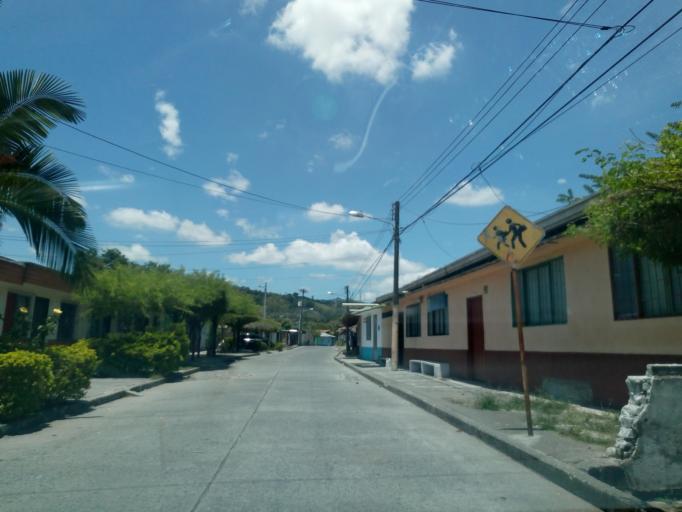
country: CO
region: Valle del Cauca
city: Cartago
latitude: 4.7292
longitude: -75.9079
